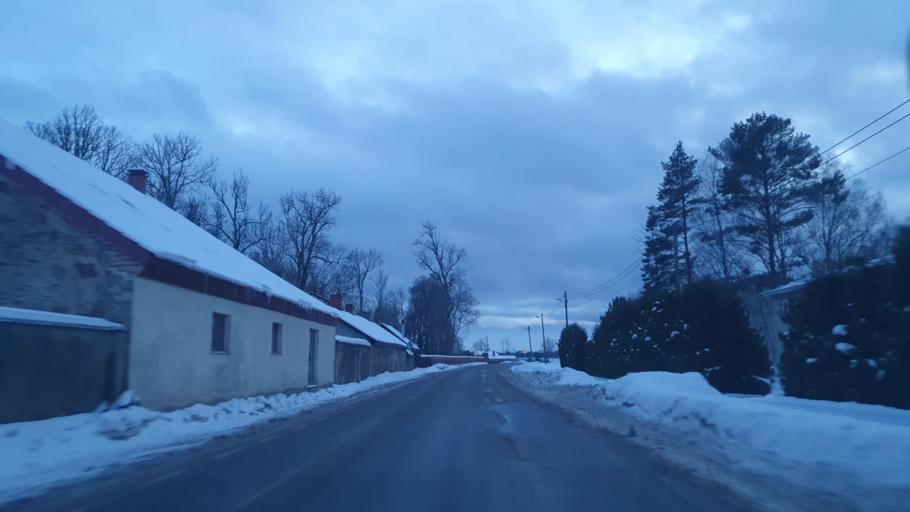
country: EE
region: Jogevamaa
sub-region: Jogeva linn
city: Jogeva
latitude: 58.5758
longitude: 26.2893
